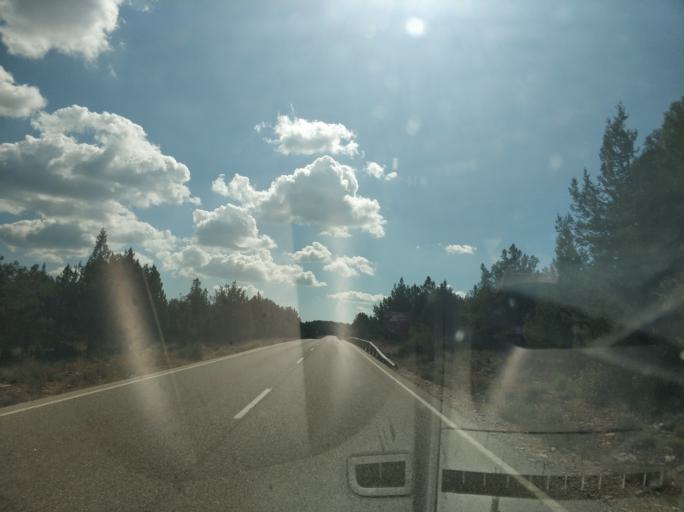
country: ES
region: Castille and Leon
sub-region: Provincia de Soria
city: Ucero
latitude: 41.7366
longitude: -3.0437
